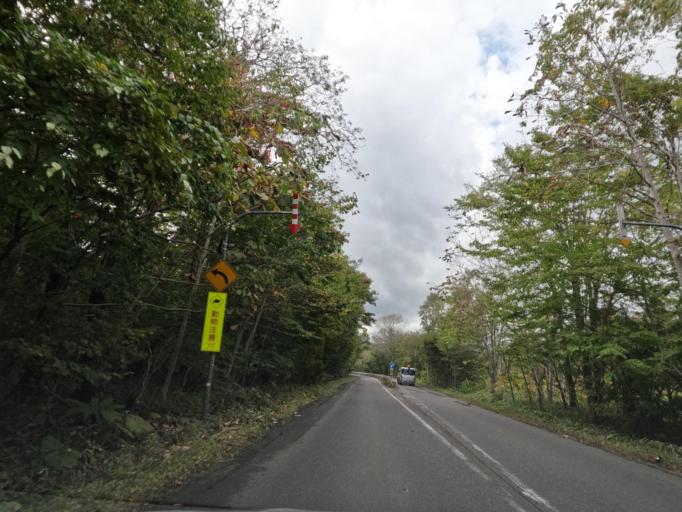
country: JP
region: Hokkaido
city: Chitose
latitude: 42.7936
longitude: 141.5081
